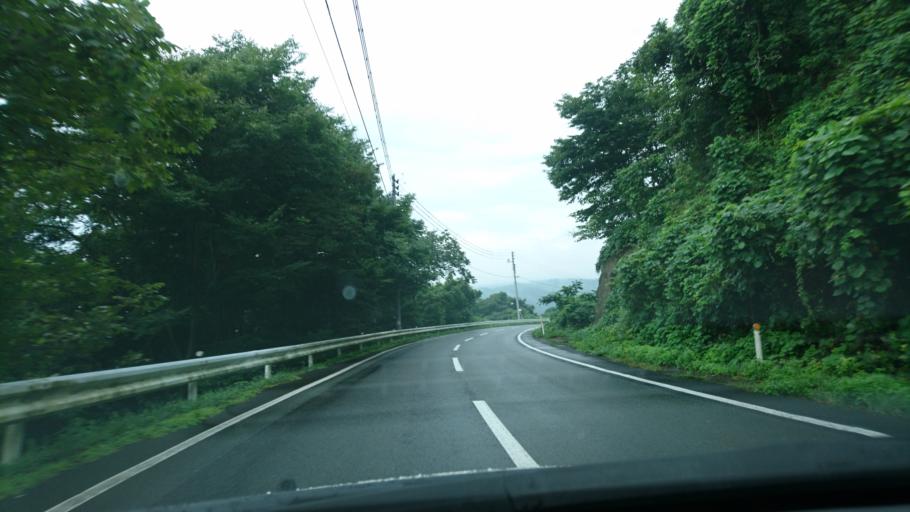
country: JP
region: Iwate
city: Ichinoseki
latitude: 38.8918
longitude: 141.2658
